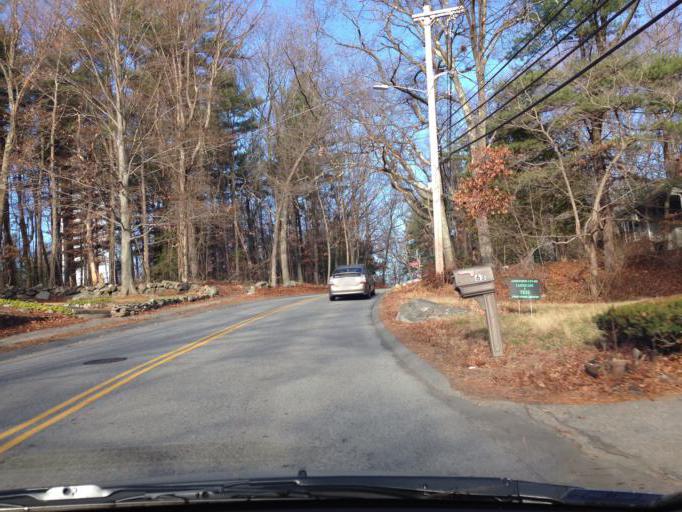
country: US
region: Massachusetts
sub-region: Middlesex County
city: Bedford
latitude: 42.5015
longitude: -71.2785
